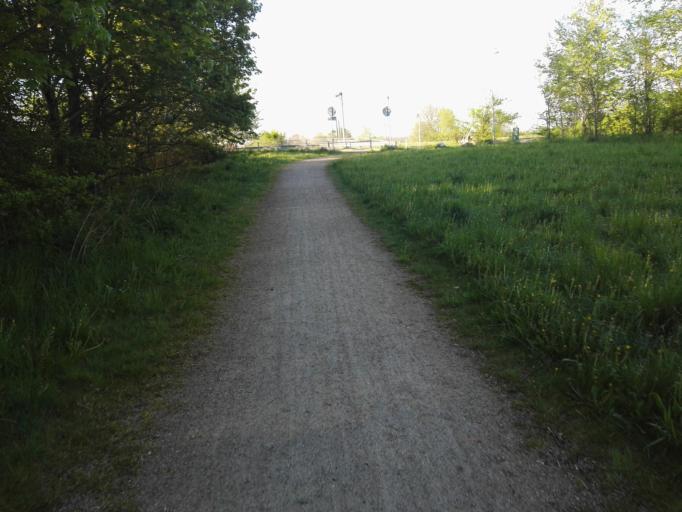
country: DK
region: Capital Region
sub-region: Ballerup Kommune
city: Malov
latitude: 55.7390
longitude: 12.3383
